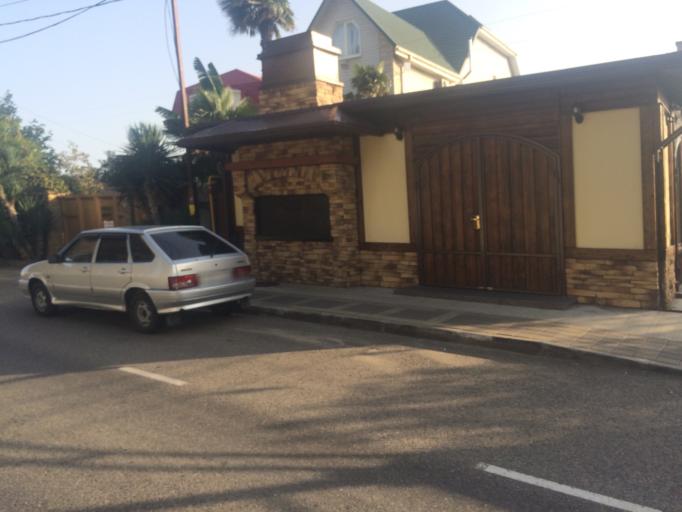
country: RU
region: Krasnodarskiy
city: Adler
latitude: 43.3886
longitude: 39.9886
